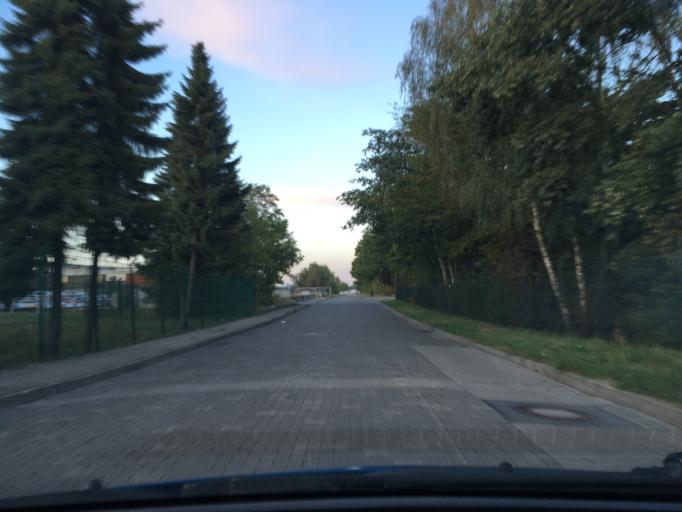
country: DE
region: Schleswig-Holstein
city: Buchhorst
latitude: 53.3688
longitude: 10.5800
